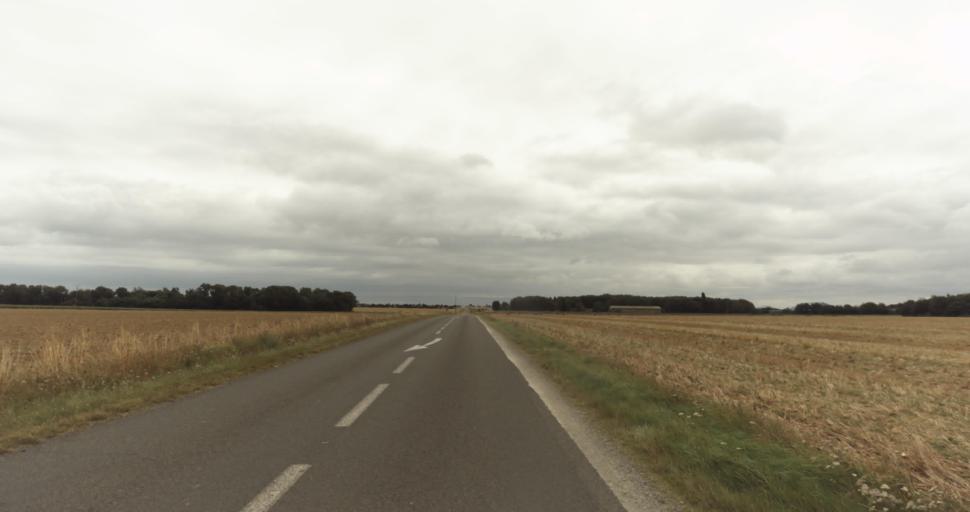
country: FR
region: Haute-Normandie
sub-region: Departement de l'Eure
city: Gravigny
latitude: 49.0500
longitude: 1.2275
